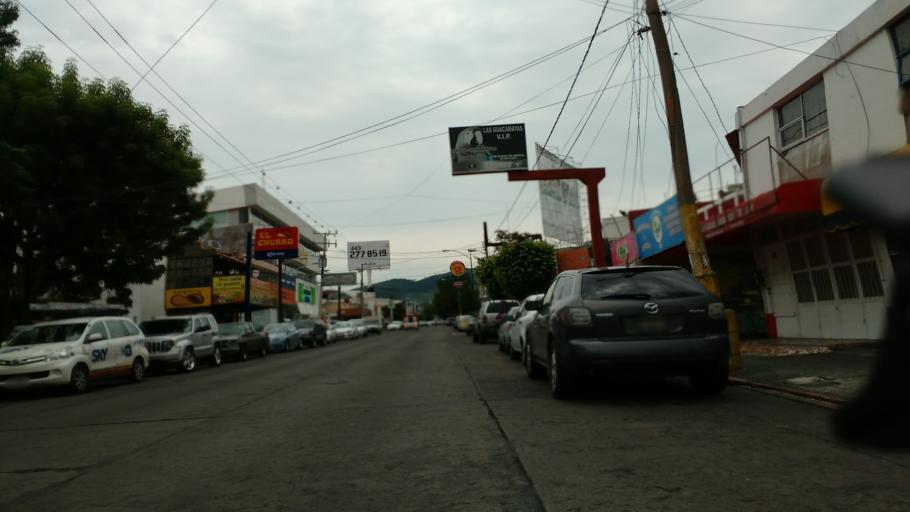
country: MX
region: Michoacan
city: Morelia
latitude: 19.6938
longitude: -101.1733
